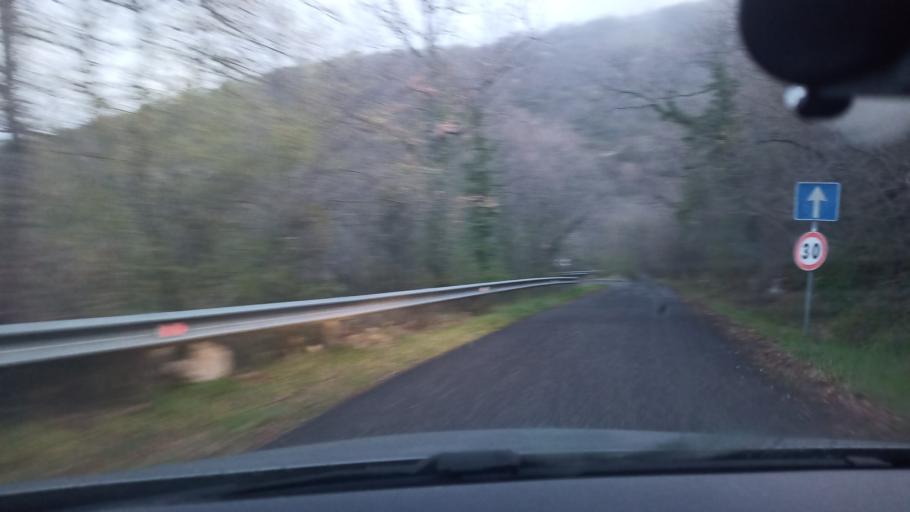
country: IT
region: Latium
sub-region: Provincia di Rieti
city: Cottanello
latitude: 42.4098
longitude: 12.6827
